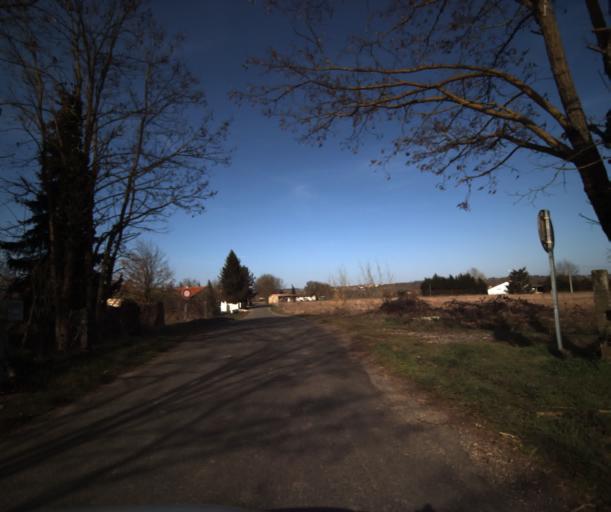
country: FR
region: Midi-Pyrenees
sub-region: Departement du Tarn-et-Garonne
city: Labastide-Saint-Pierre
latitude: 43.9281
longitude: 1.3549
